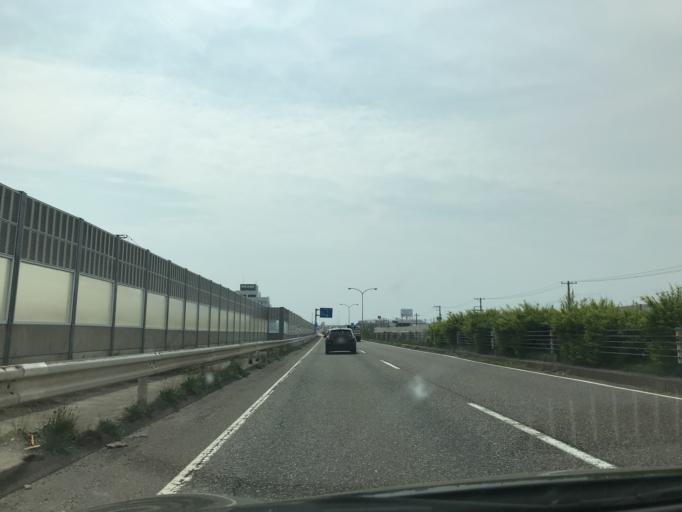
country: JP
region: Niigata
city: Kameda-honcho
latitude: 37.8872
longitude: 139.0774
